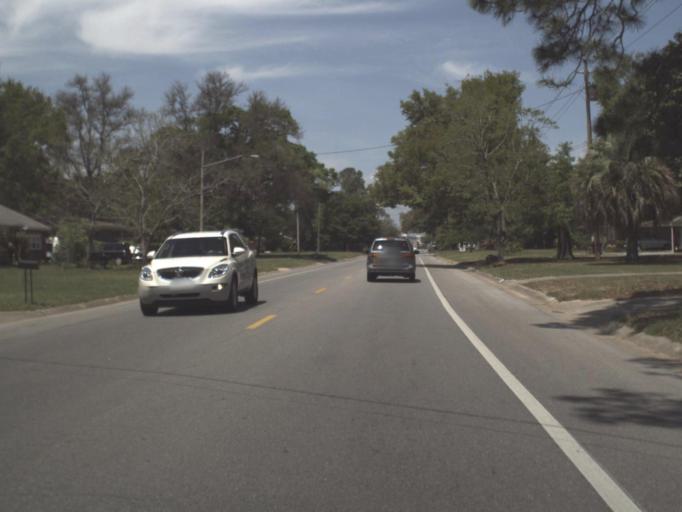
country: US
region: Florida
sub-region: Escambia County
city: Goulding
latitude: 30.4617
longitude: -87.2015
